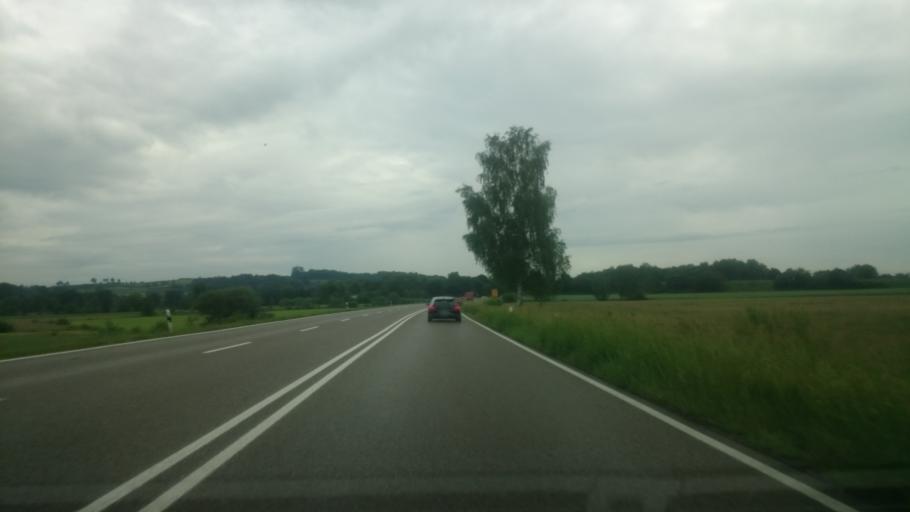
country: DE
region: Bavaria
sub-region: Upper Bavaria
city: Pornbach
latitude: 48.6188
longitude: 11.4413
